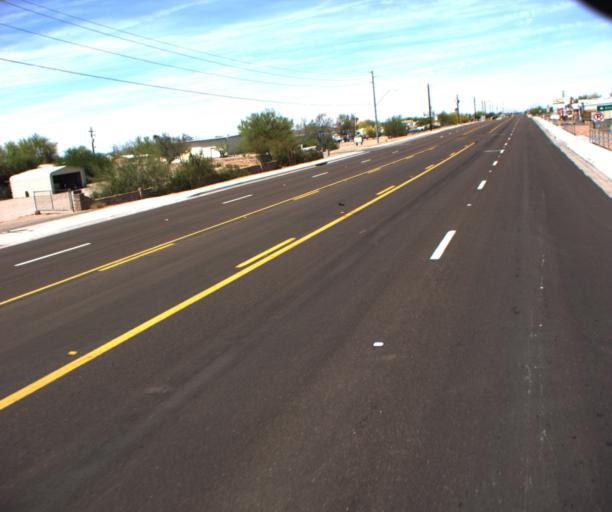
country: US
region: Arizona
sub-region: La Paz County
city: Quartzsite
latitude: 33.6760
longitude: -114.2170
